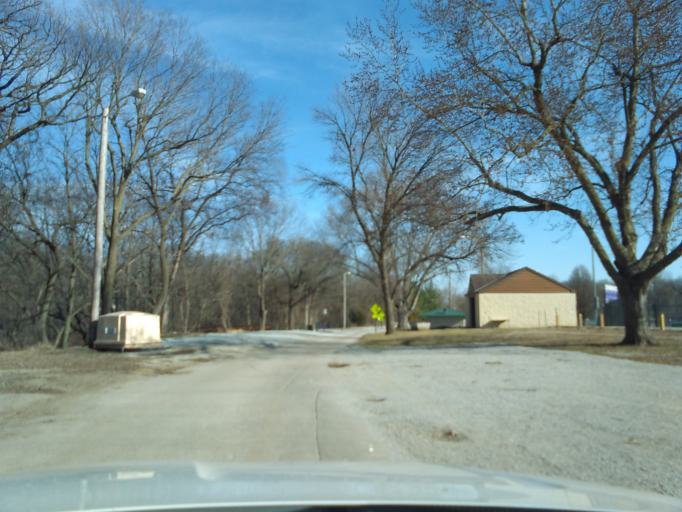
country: US
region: Nebraska
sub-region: Otoe County
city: Nebraska City
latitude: 40.6757
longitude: -95.8763
